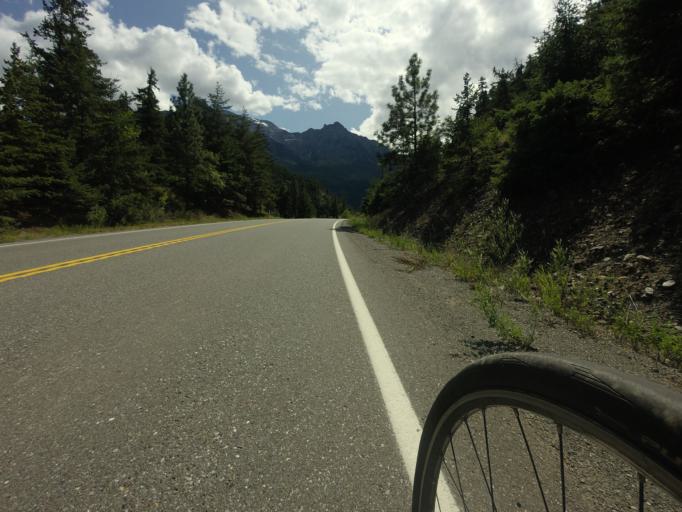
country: CA
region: British Columbia
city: Lillooet
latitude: 50.6602
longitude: -121.9921
